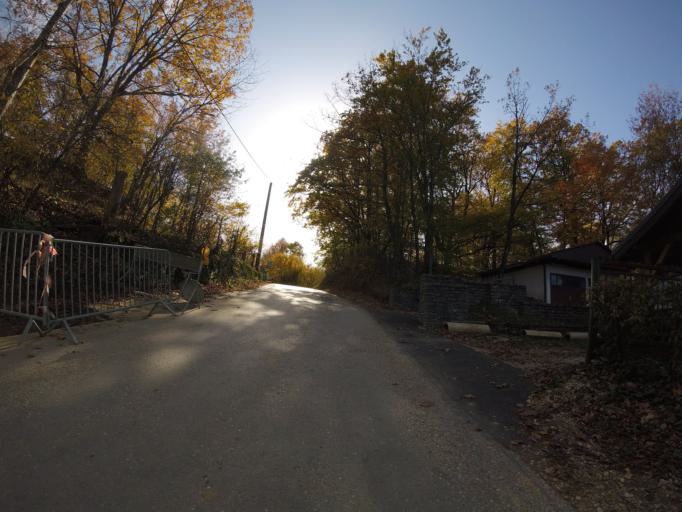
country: HR
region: Zagrebacka
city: Gradici
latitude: 45.6169
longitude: 16.0172
